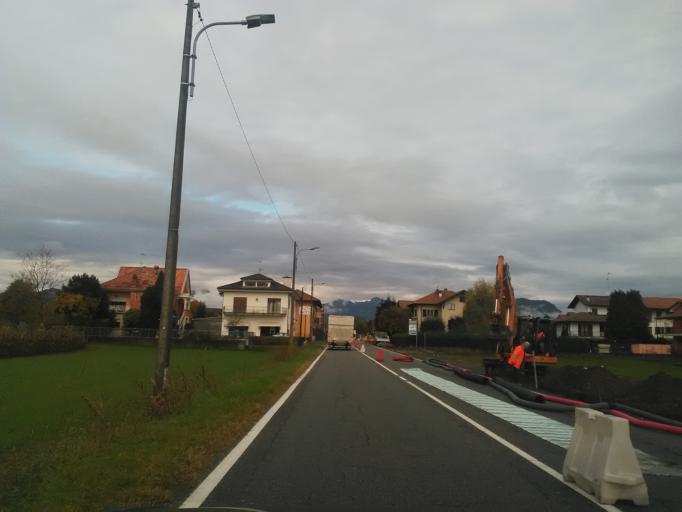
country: IT
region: Piedmont
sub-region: Provincia di Novara
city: Prato Sesia
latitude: 45.6516
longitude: 8.3696
